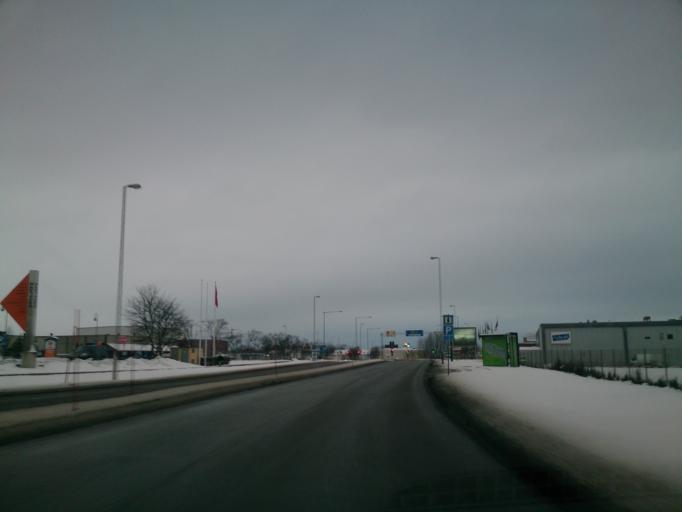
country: SE
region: OEstergoetland
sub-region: Linkopings Kommun
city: Linkoping
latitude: 58.4229
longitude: 15.6164
